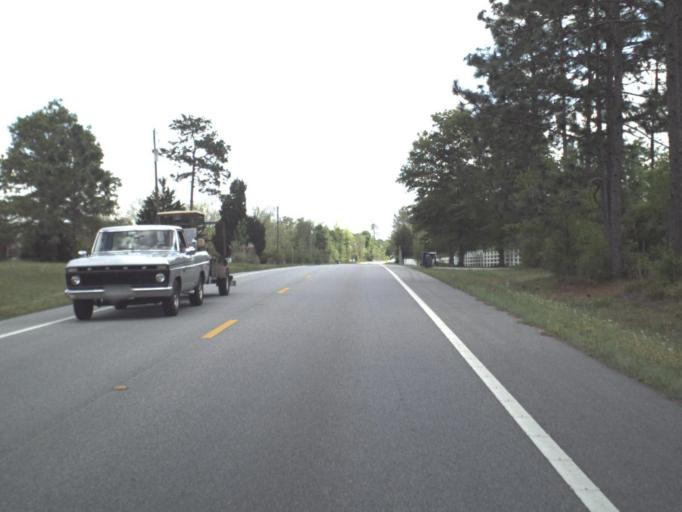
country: US
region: Florida
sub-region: Escambia County
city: Molino
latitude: 30.7891
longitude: -87.4120
